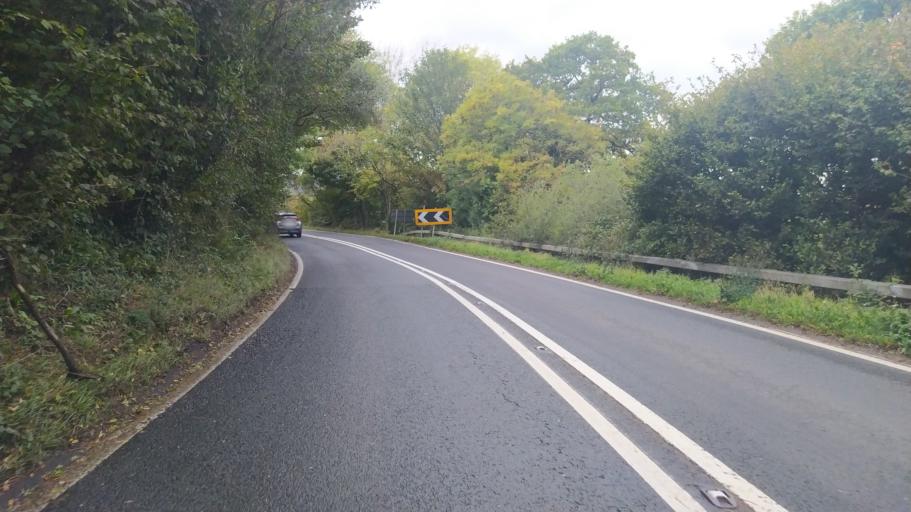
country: GB
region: England
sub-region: Dorset
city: Lyme Regis
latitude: 50.7432
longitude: -2.8592
